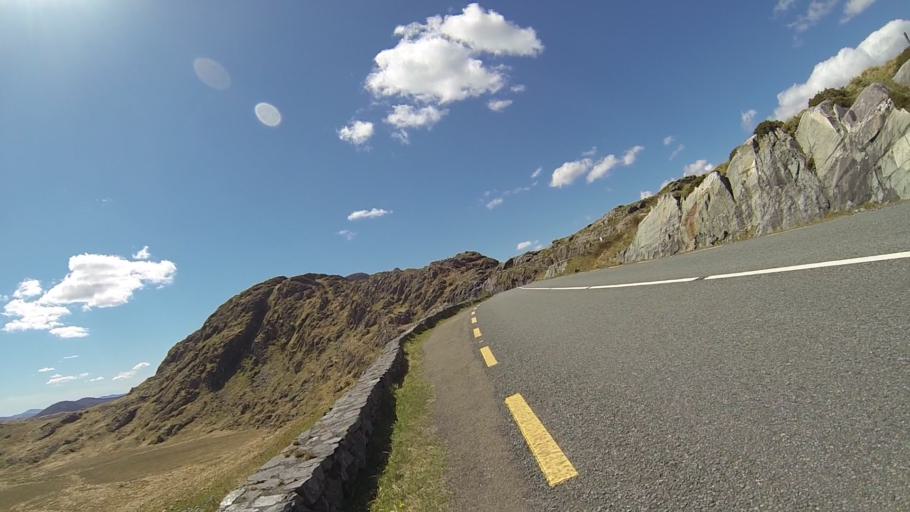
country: IE
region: Munster
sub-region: Ciarrai
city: Kenmare
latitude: 51.9380
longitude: -9.6543
